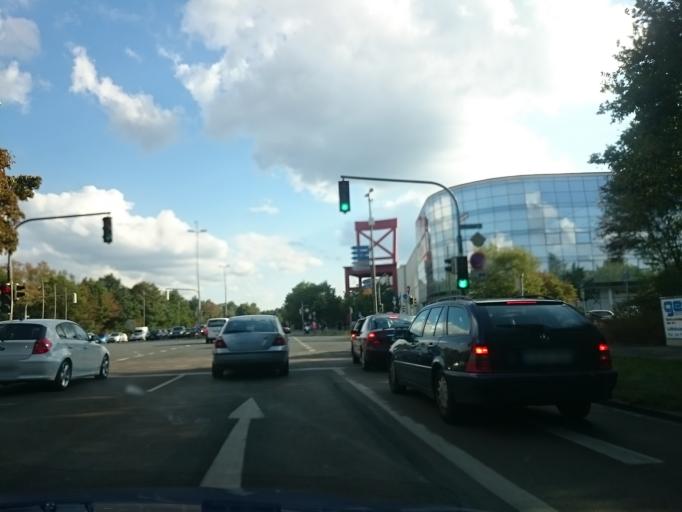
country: DE
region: Bavaria
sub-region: Regierungsbezirk Mittelfranken
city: Nuernberg
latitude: 49.4318
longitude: 11.1028
